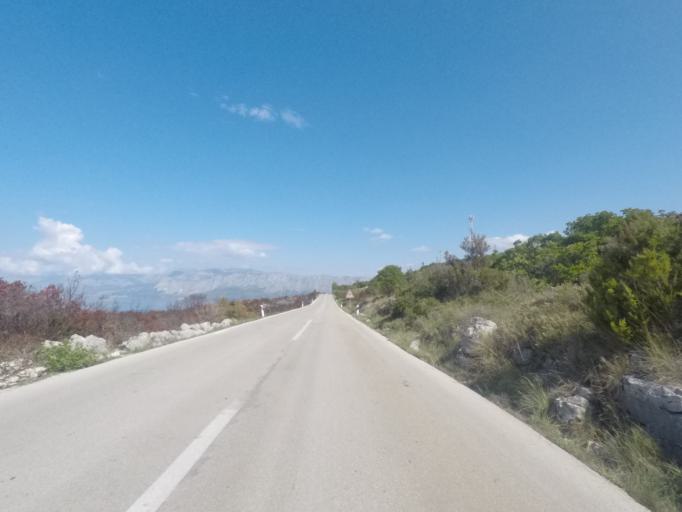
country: HR
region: Dubrovacko-Neretvanska
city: Orebic
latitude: 43.1280
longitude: 17.1241
